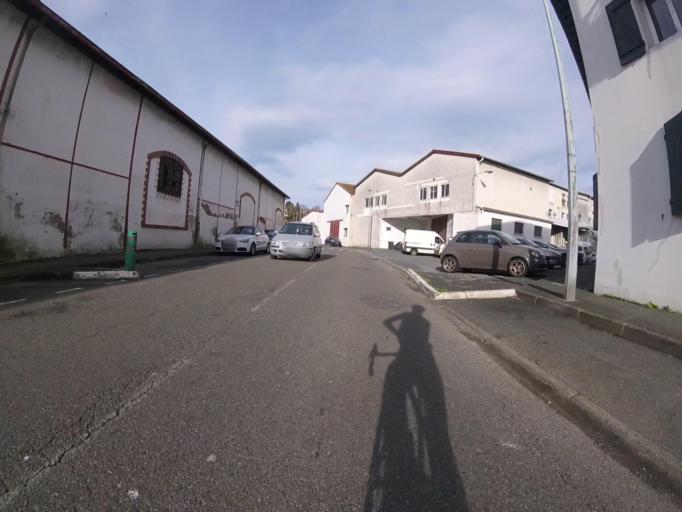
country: FR
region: Aquitaine
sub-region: Departement des Pyrenees-Atlantiques
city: Saint-Jean-de-Luz
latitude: 43.3820
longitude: -1.6652
